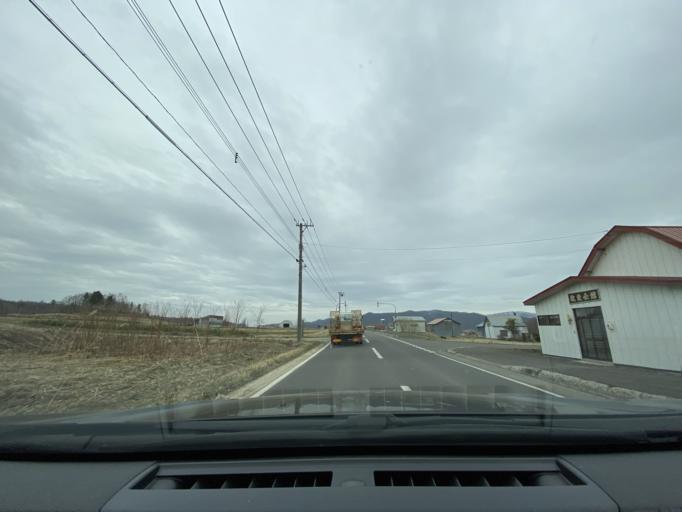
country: JP
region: Hokkaido
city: Nayoro
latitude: 44.1014
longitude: 142.4759
